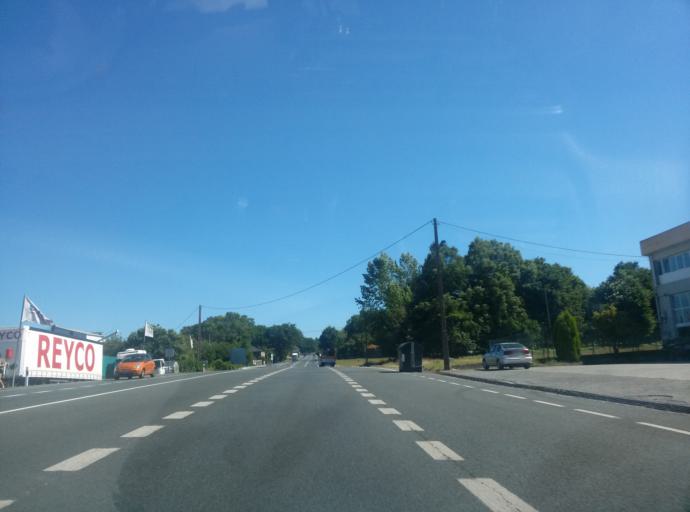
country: ES
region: Galicia
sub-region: Provincia de Lugo
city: Outeiro de Rei
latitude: 43.0579
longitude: -7.5984
